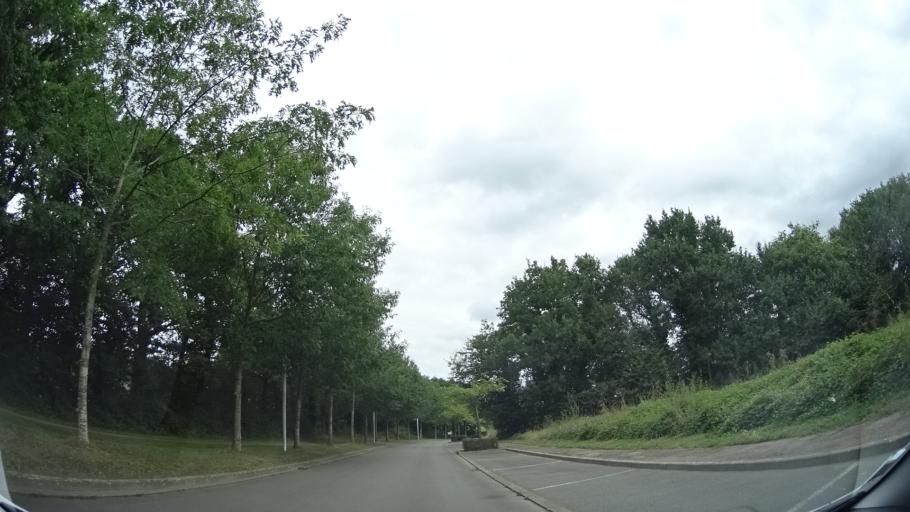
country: FR
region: Brittany
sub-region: Departement d'Ille-et-Vilaine
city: Bruz
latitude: 48.0476
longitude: -1.7464
